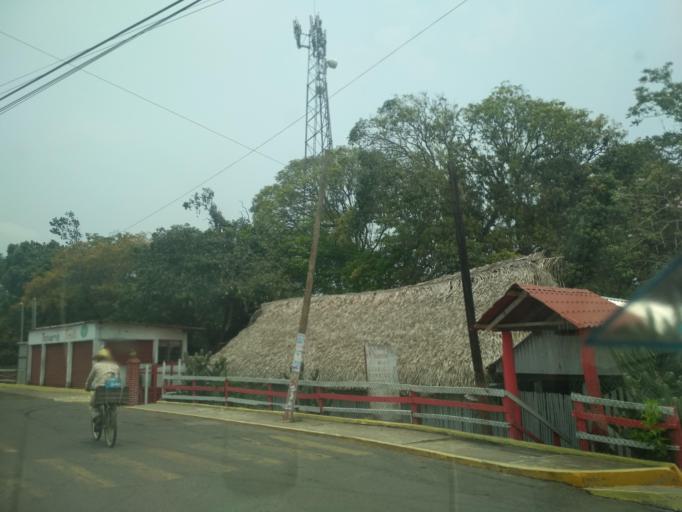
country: MX
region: Veracruz
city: El Tejar
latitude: 19.0582
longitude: -96.1582
